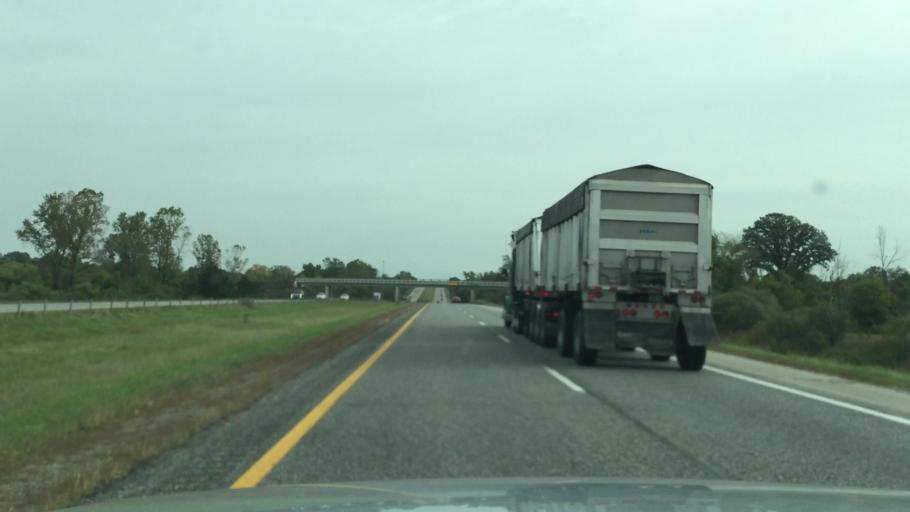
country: US
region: Michigan
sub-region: Shiawassee County
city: Durand
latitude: 42.9020
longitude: -84.0723
